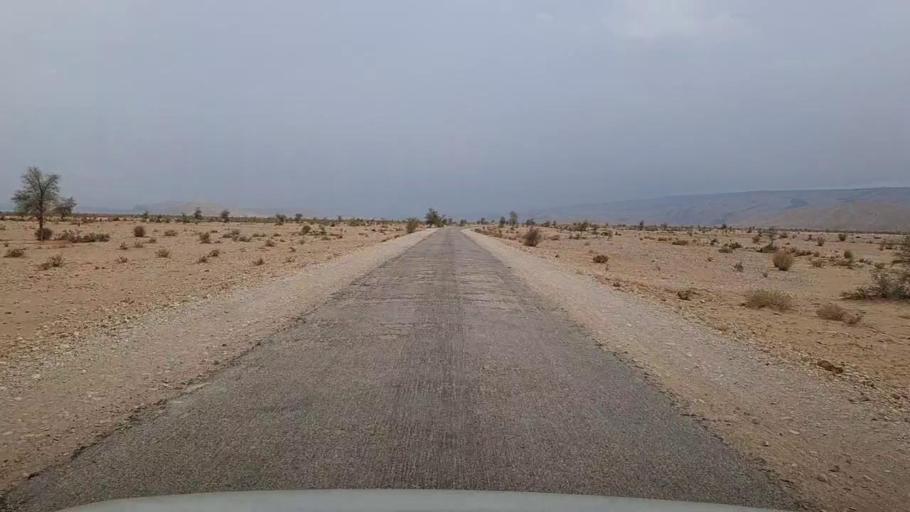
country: PK
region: Sindh
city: Sehwan
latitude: 26.2681
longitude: 67.7237
